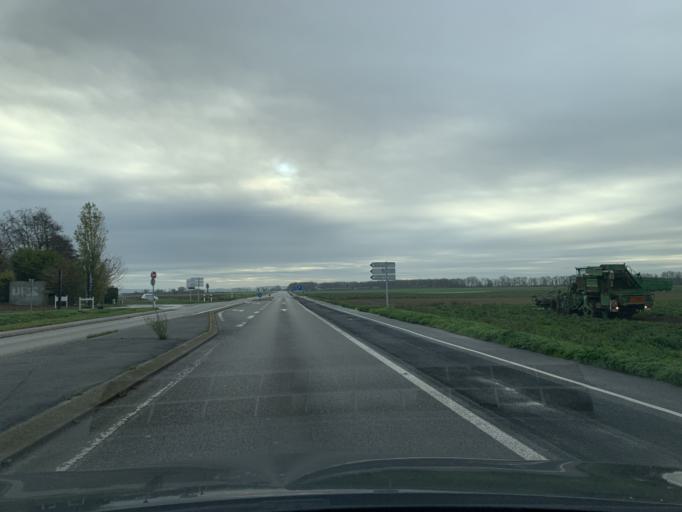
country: FR
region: Nord-Pas-de-Calais
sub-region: Departement du Nord
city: Goeulzin
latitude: 50.3367
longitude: 3.1000
